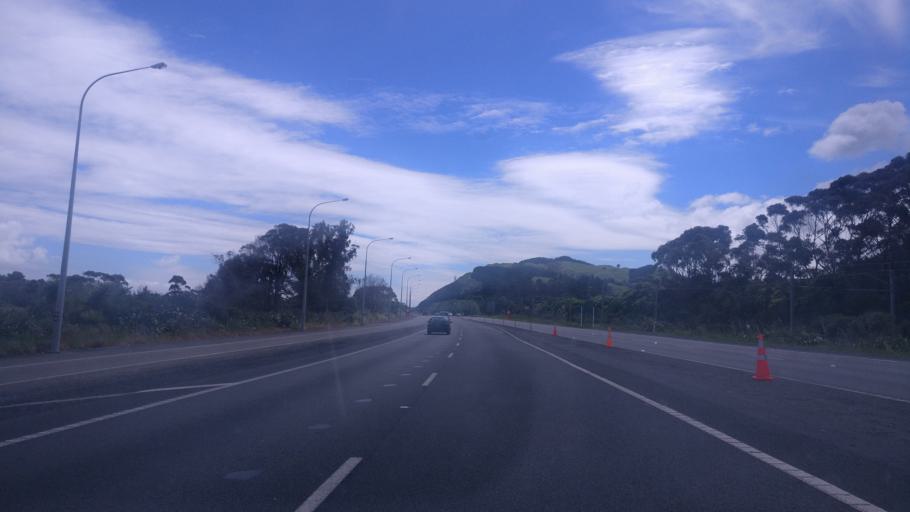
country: NZ
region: Wellington
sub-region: Kapiti Coast District
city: Paraparaumu
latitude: -40.9653
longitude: 174.9860
